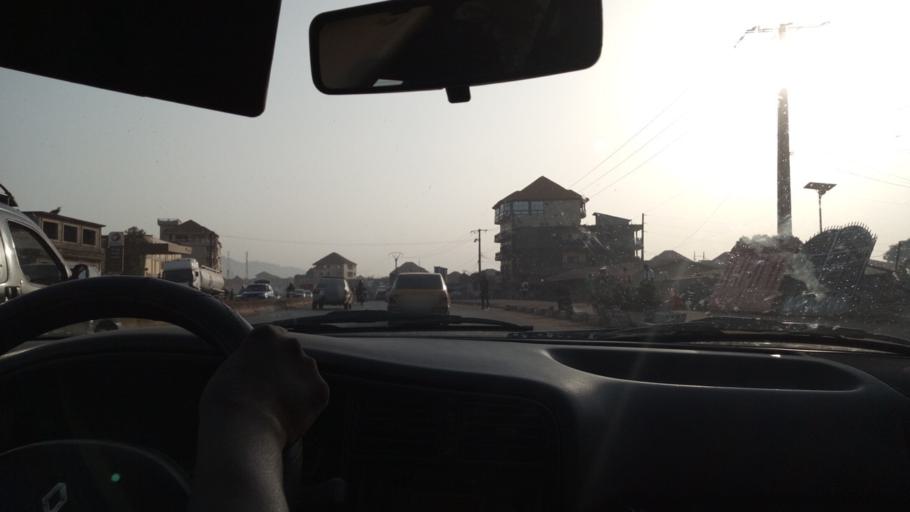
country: GN
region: Kindia
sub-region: Prefecture de Dubreka
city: Dubreka
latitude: 9.6745
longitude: -13.5464
